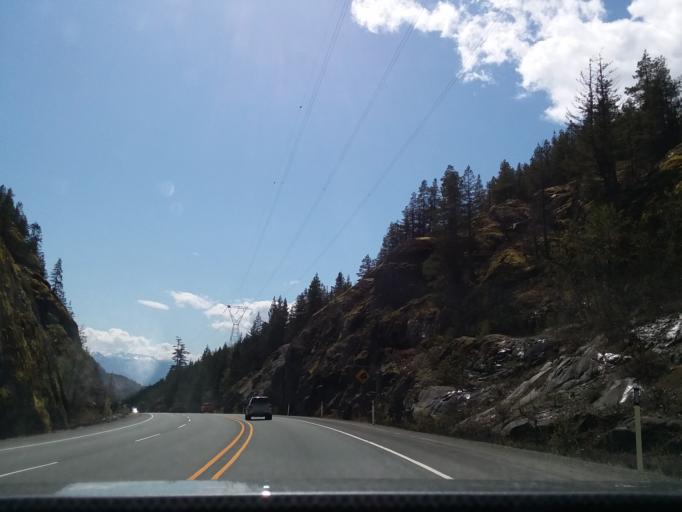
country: CA
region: British Columbia
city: Whistler
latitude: 49.9043
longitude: -123.1633
